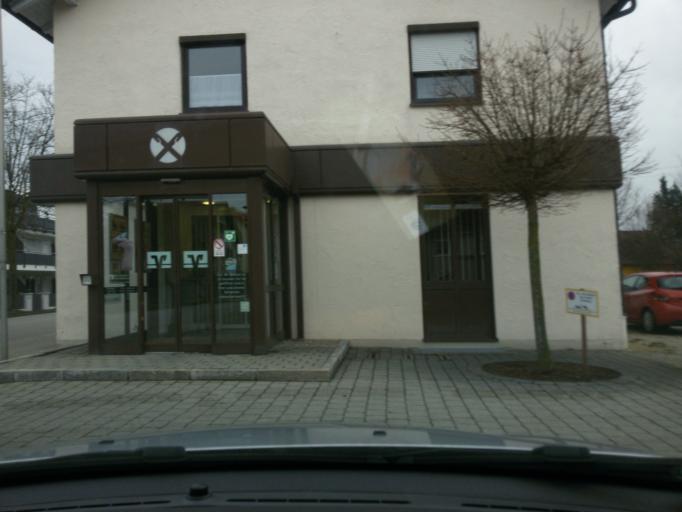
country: DE
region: Bavaria
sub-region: Swabia
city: Graben
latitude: 48.1885
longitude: 10.8233
